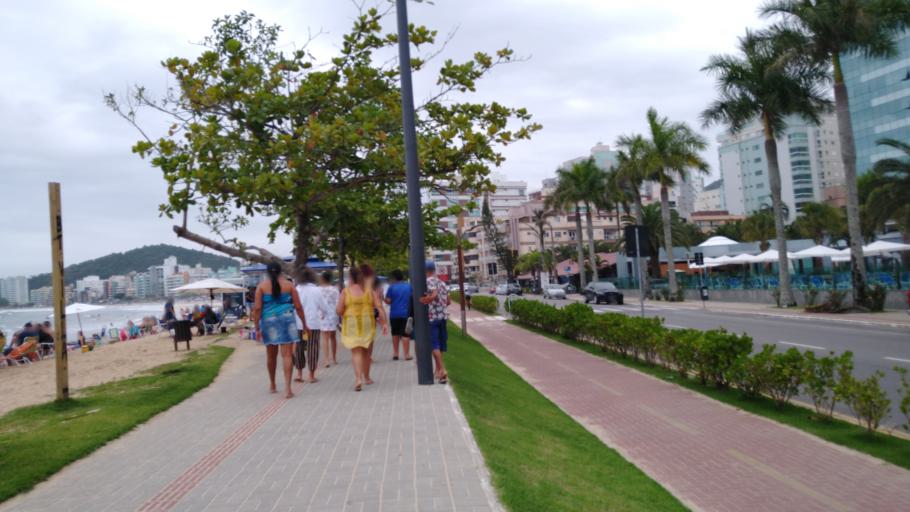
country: BR
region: Santa Catarina
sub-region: Itapema
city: Itapema
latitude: -27.0961
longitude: -48.6129
